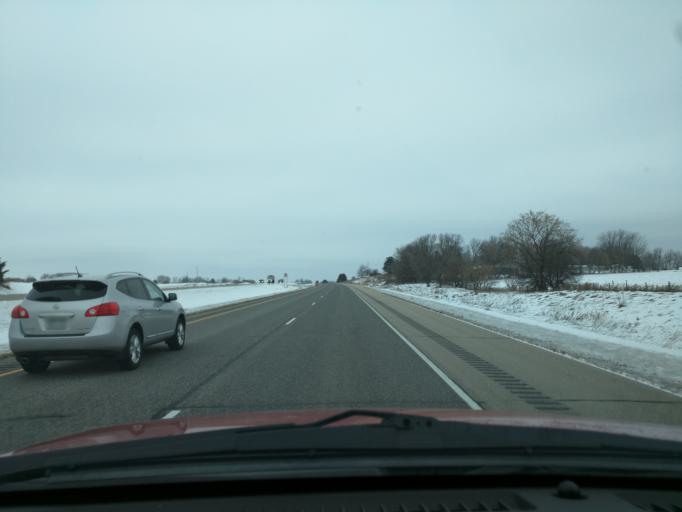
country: US
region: Minnesota
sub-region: Winona County
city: Winona
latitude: 43.9379
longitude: -91.6286
